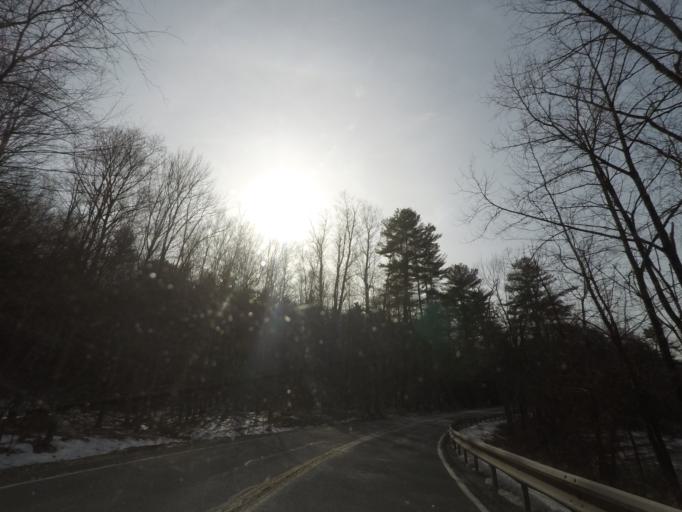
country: US
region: New York
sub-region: Rensselaer County
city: Nassau
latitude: 42.4863
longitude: -73.5586
